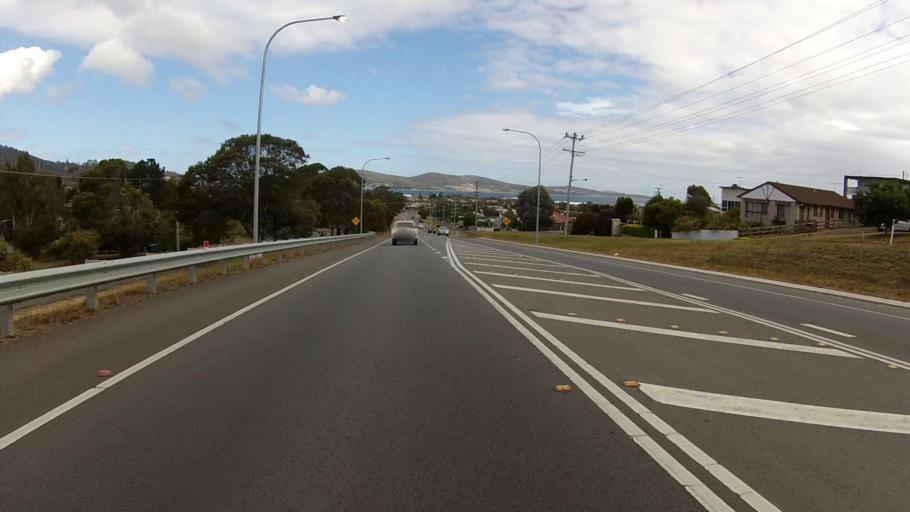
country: AU
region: Tasmania
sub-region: Clarence
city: Rokeby
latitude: -42.8910
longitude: 147.4343
